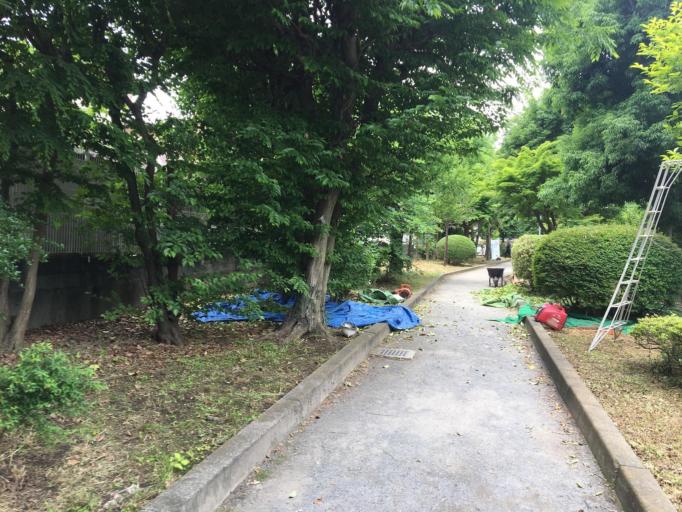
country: JP
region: Tokyo
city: Chofugaoka
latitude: 35.6415
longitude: 139.5811
